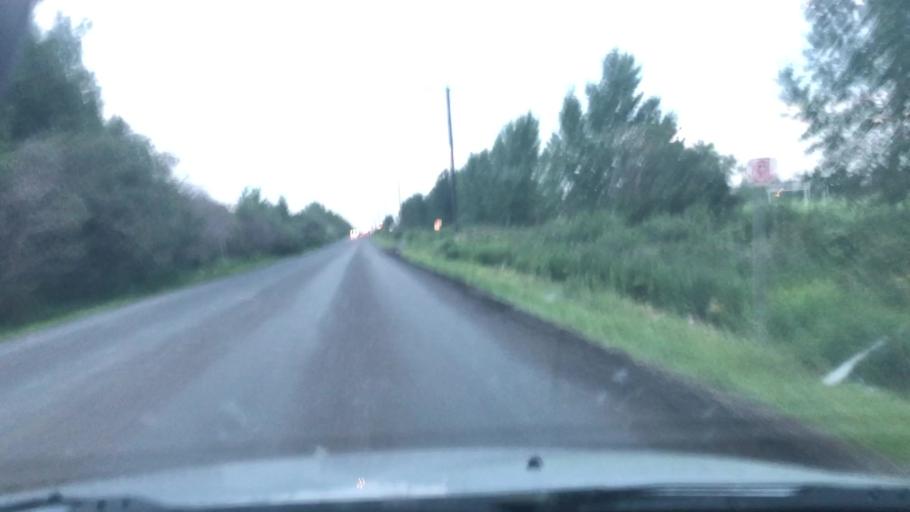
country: CA
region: Alberta
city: Devon
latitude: 53.4908
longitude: -113.6889
